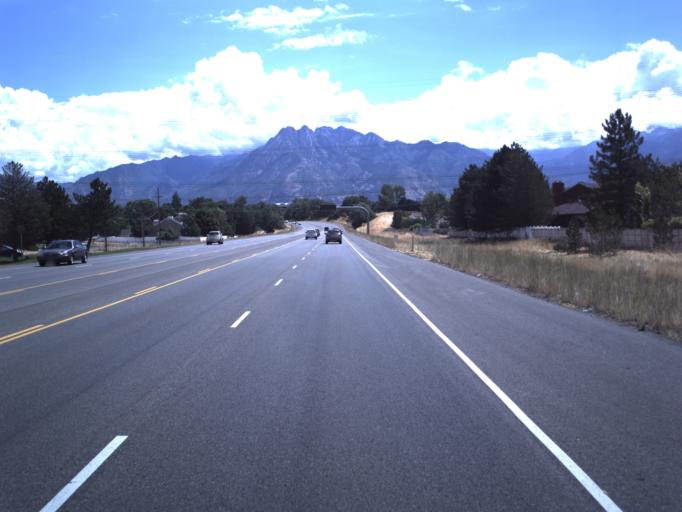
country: US
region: Utah
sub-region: Salt Lake County
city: Taylorsville
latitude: 40.6530
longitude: -111.9208
